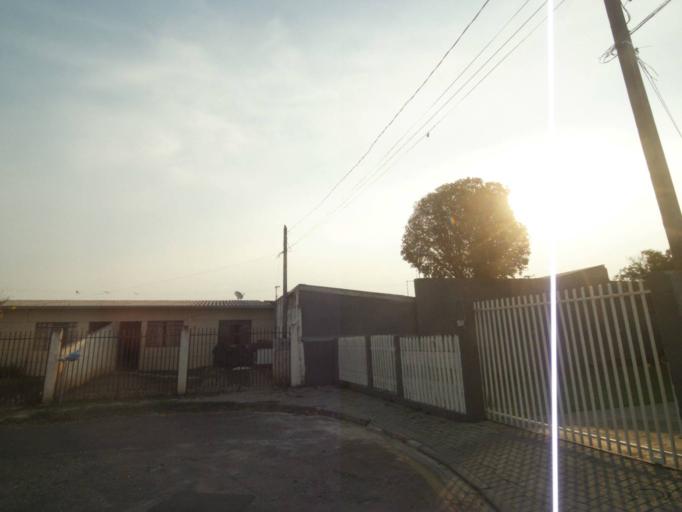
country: BR
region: Parana
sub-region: Sao Jose Dos Pinhais
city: Sao Jose dos Pinhais
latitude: -25.5257
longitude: -49.2701
